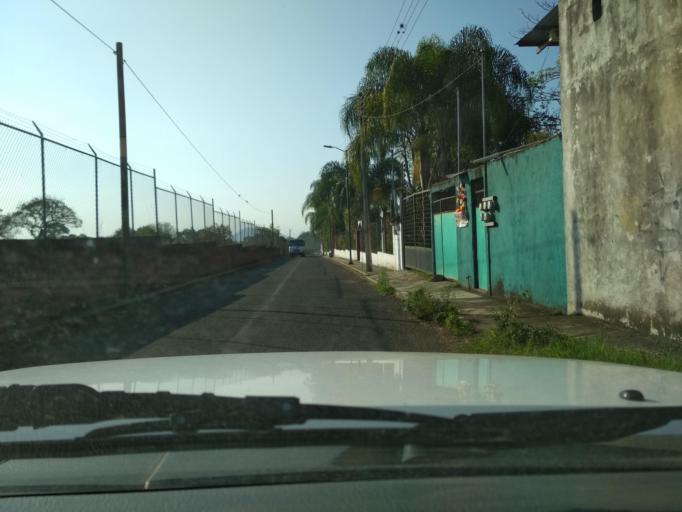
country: MX
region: Veracruz
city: Cordoba
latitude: 18.8713
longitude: -96.9328
